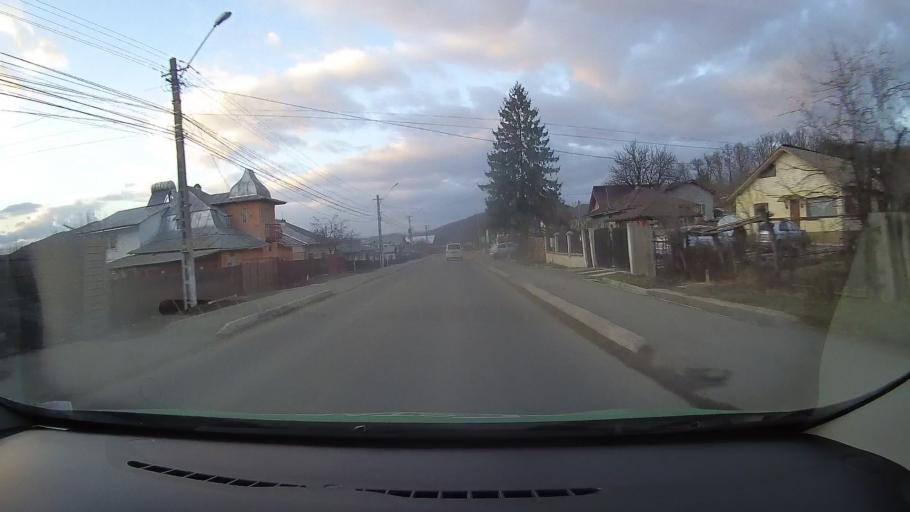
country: RO
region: Dambovita
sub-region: Municipiul Moreni
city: Moreni
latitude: 45.0004
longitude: 25.6473
